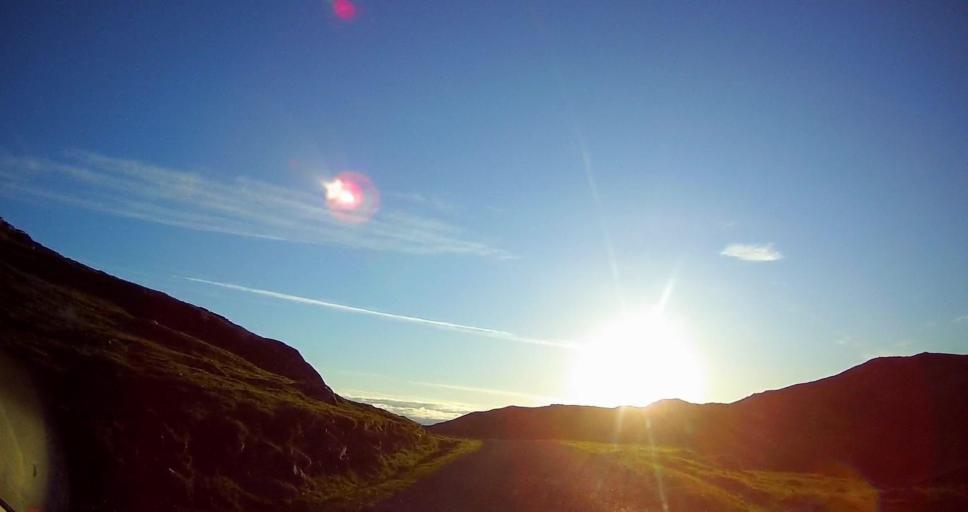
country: GB
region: Scotland
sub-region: Shetland Islands
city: Lerwick
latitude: 60.4488
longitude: -1.4201
